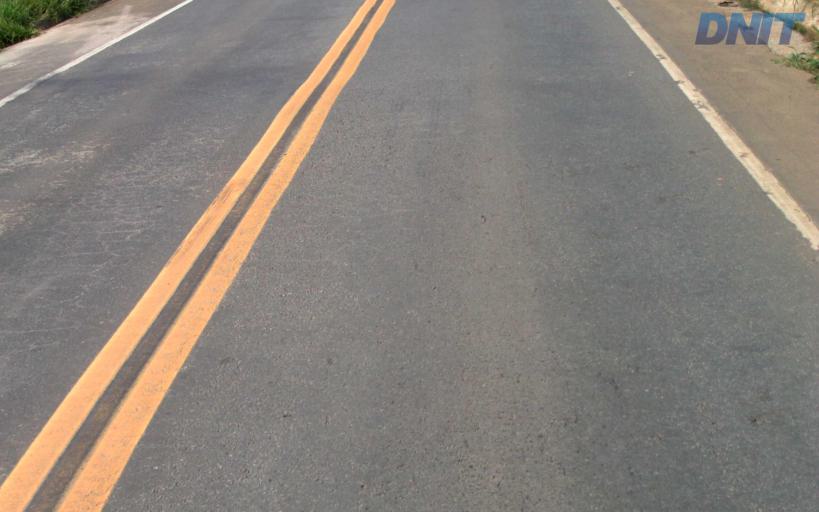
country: BR
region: Minas Gerais
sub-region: Belo Oriente
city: Belo Oriente
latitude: -19.1995
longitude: -42.2867
